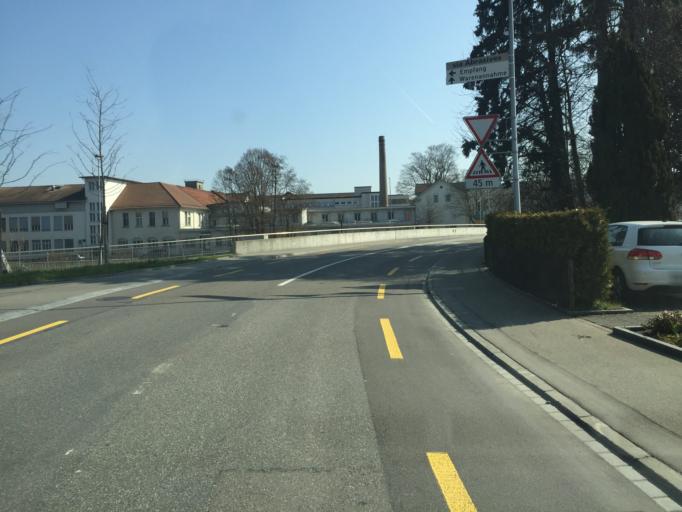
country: CH
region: Thurgau
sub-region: Frauenfeld District
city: Frauenfeld
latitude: 47.5609
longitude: 8.8971
